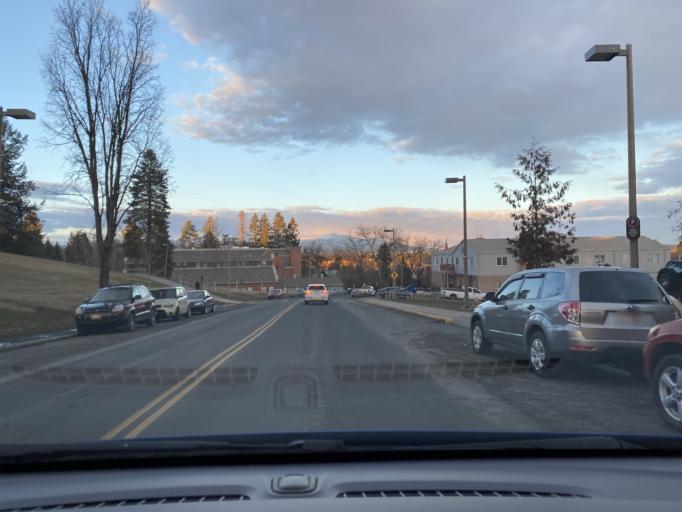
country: US
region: Idaho
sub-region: Latah County
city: Moscow
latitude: 46.7237
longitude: -117.0114
